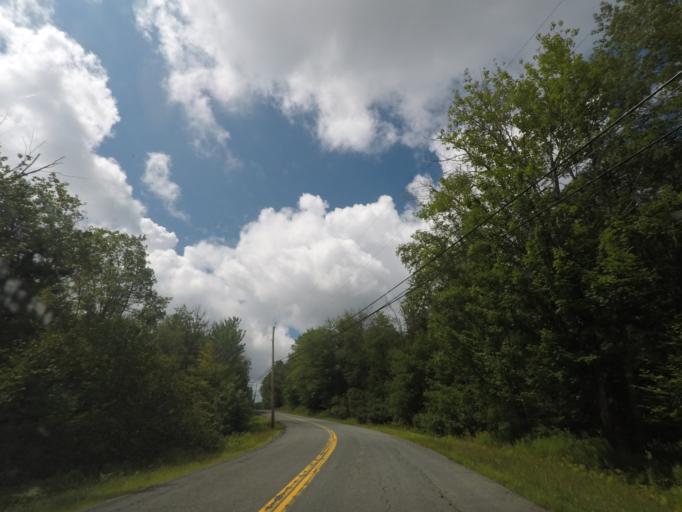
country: US
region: New York
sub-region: Rensselaer County
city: Averill Park
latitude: 42.6422
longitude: -73.4359
